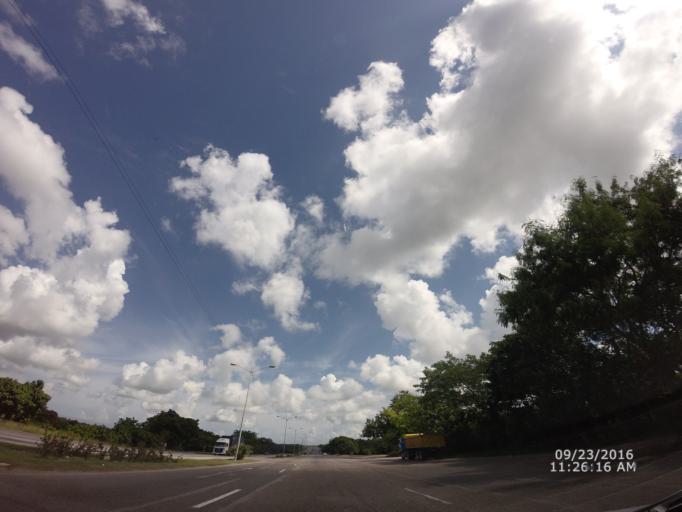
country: CU
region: La Habana
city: San Miguel del Padron
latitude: 23.0729
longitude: -82.2732
